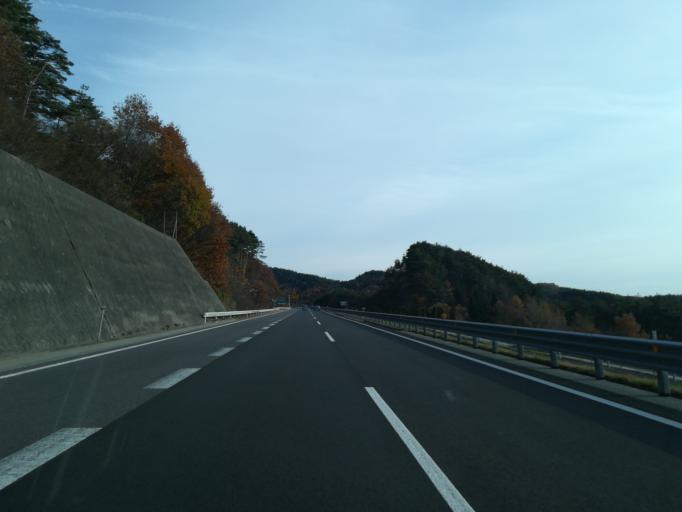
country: JP
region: Nagano
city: Saku
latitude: 36.2737
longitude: 138.5181
